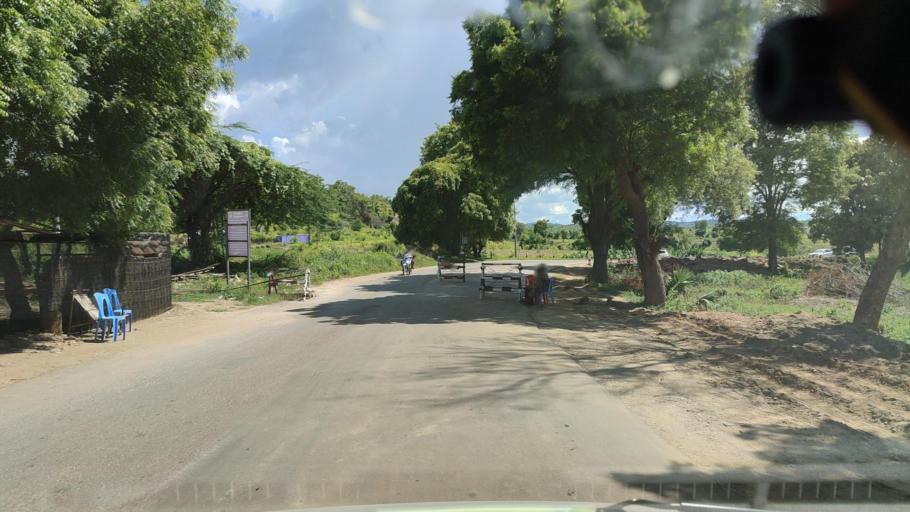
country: MM
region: Magway
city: Magway
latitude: 19.9878
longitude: 94.9932
